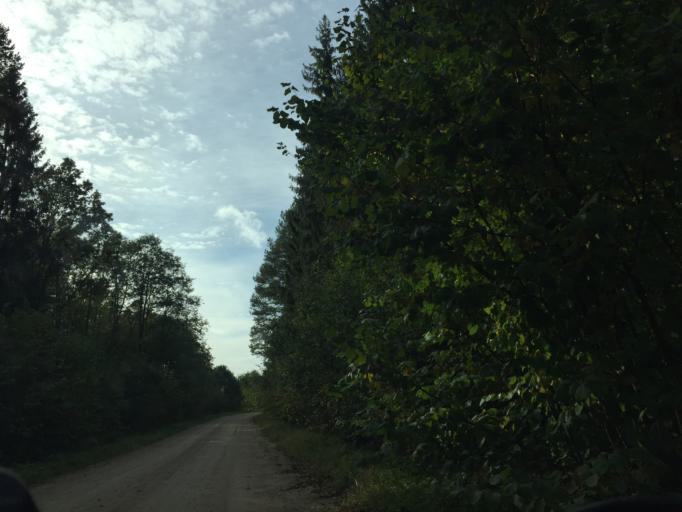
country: LV
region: Jaunpils
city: Jaunpils
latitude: 56.6121
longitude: 23.0144
